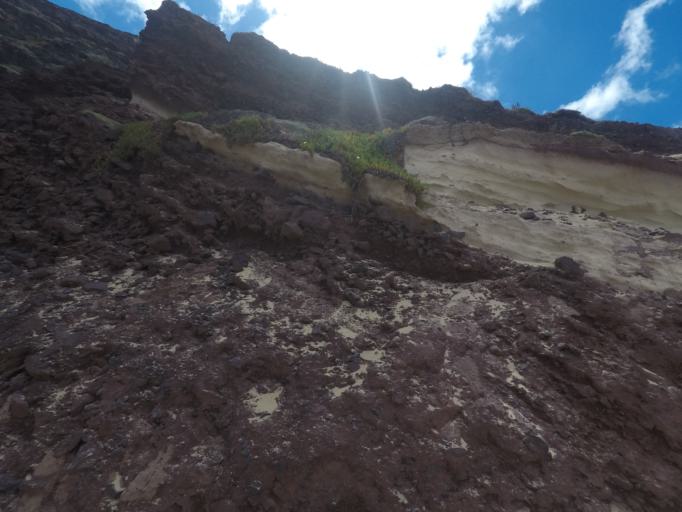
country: PT
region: Madeira
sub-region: Porto Santo
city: Vila de Porto Santo
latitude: 33.0622
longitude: -16.2957
